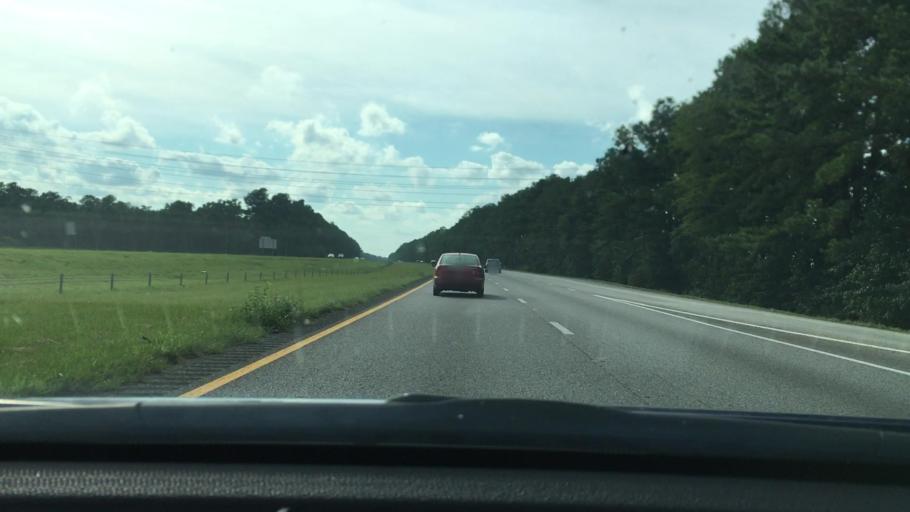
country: US
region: South Carolina
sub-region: Dorchester County
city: Summerville
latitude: 33.0831
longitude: -80.2088
